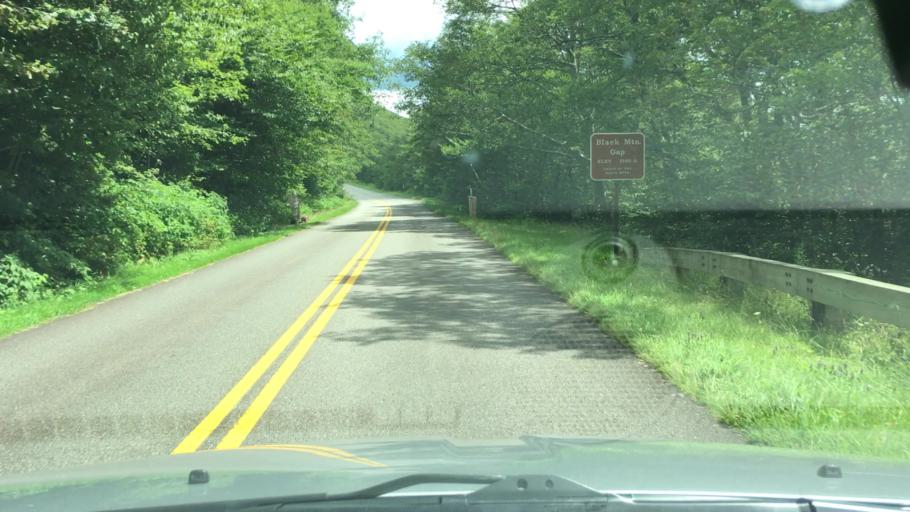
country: US
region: North Carolina
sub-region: Buncombe County
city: Black Mountain
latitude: 35.7193
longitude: -82.2809
